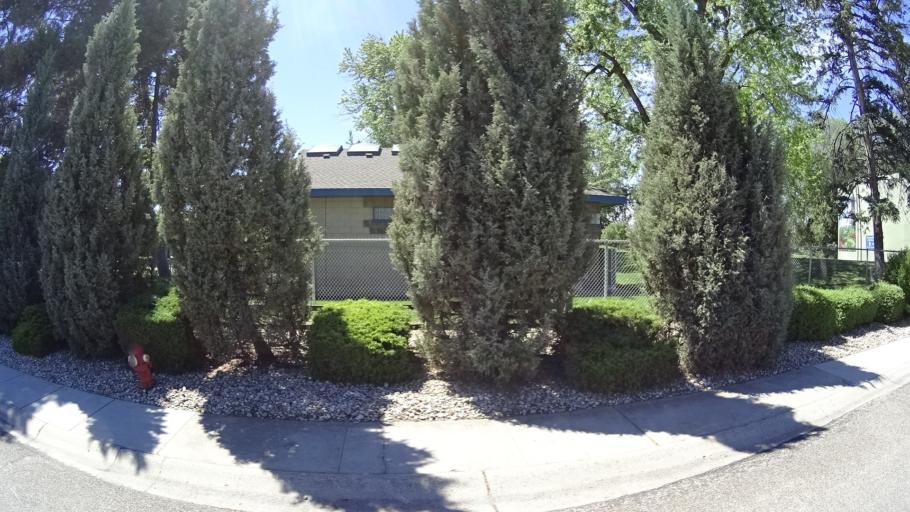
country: US
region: Idaho
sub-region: Ada County
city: Garden City
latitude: 43.5828
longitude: -116.2346
